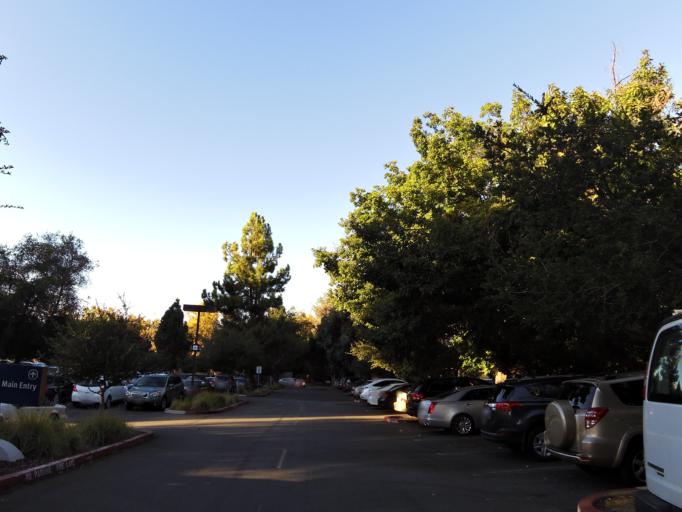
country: US
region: California
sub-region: Santa Clara County
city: Mountain View
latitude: 37.3686
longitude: -122.0783
